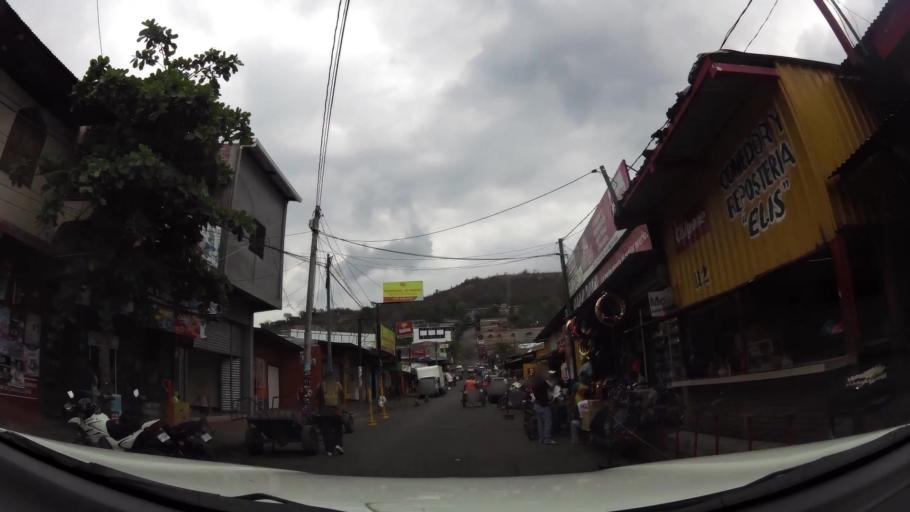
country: NI
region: Matagalpa
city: Matagalpa
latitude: 12.9352
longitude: -85.9124
